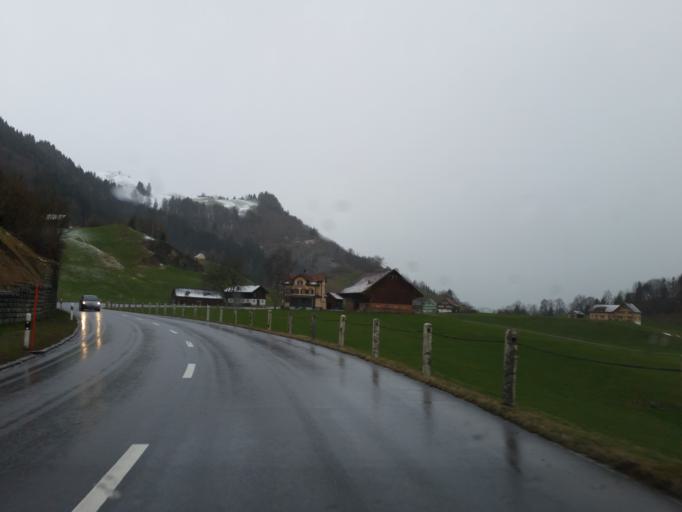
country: CH
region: Appenzell Innerrhoden
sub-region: Appenzell Inner Rhodes
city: Appenzell
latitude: 47.3417
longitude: 9.3909
